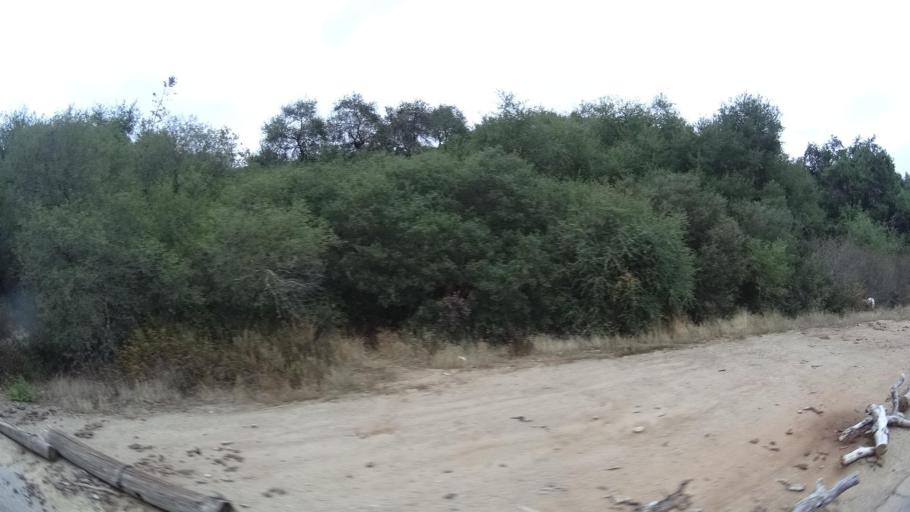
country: US
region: California
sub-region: San Diego County
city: Escondido
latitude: 33.0843
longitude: -117.1146
